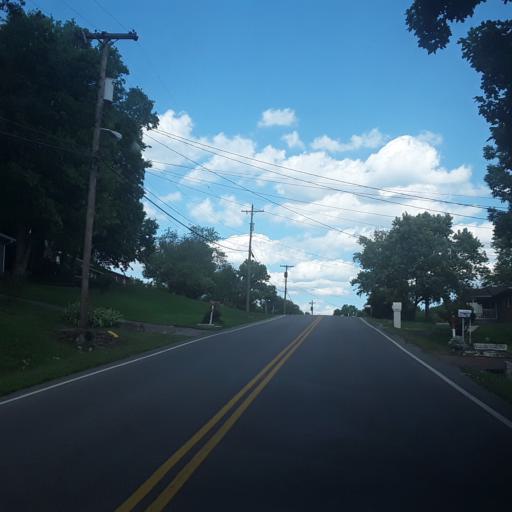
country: US
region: Tennessee
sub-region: Davidson County
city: Lakewood
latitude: 36.2013
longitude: -86.6302
